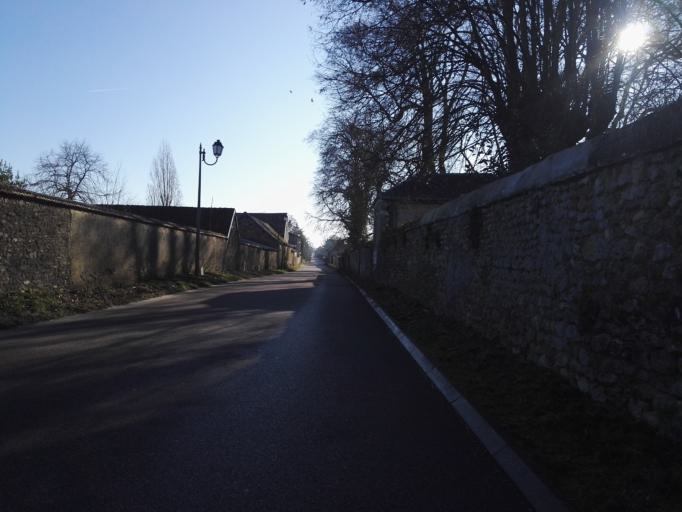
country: FR
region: Haute-Normandie
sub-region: Departement de l'Eure
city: Pacy-sur-Eure
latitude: 49.0084
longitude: 1.4176
